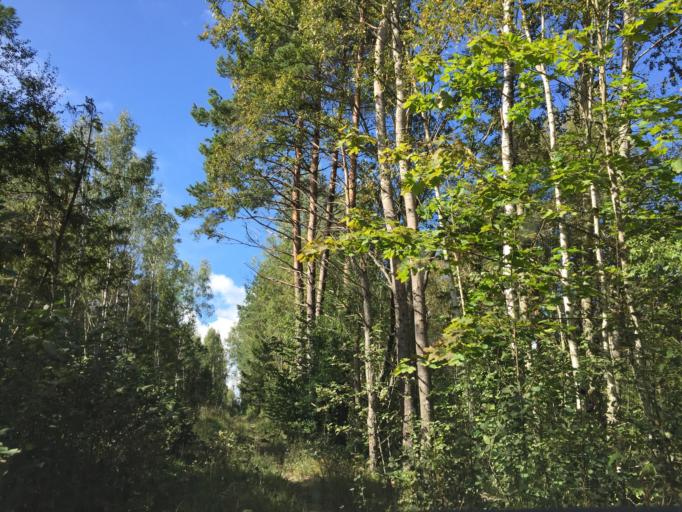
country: LV
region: Kuldigas Rajons
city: Kuldiga
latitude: 56.9799
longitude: 21.8966
